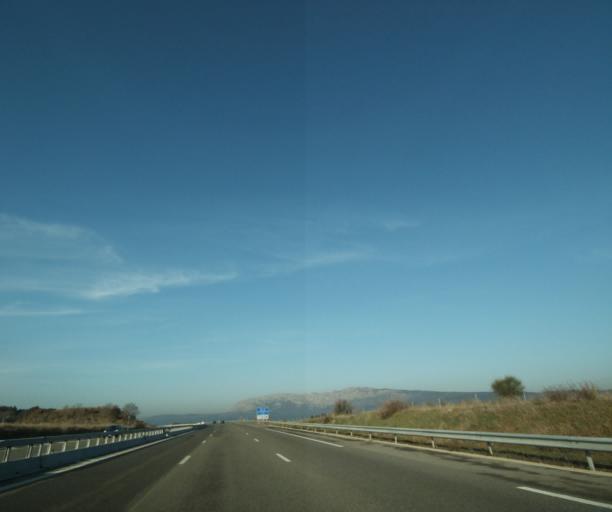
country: FR
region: Provence-Alpes-Cote d'Azur
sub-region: Departement du Var
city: Pourrieres
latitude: 43.4808
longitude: 5.7437
